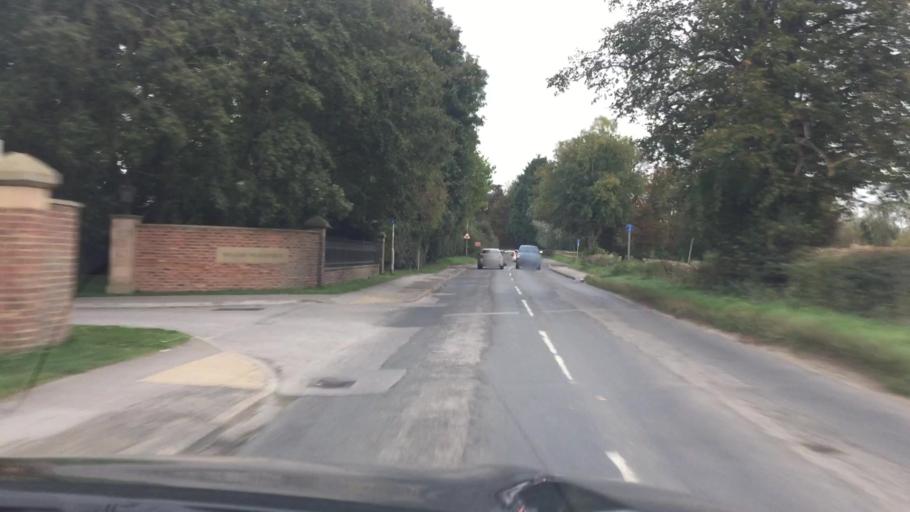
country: GB
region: England
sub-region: East Riding of Yorkshire
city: Pocklington
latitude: 53.9238
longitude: -0.7872
